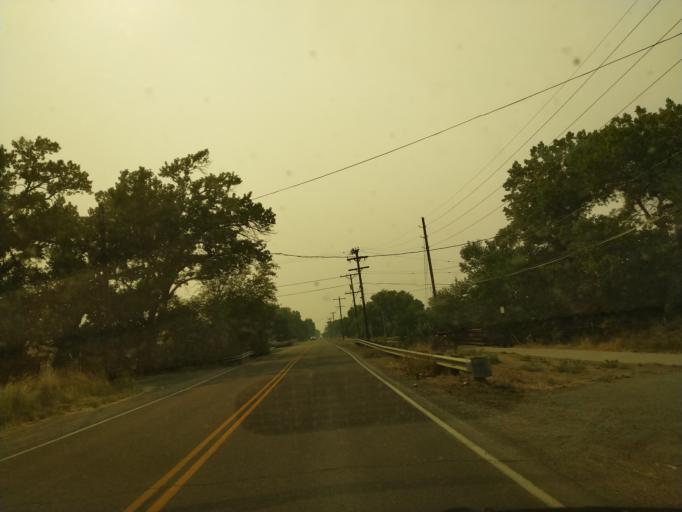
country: US
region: Colorado
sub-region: Mesa County
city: Fruitvale
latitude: 39.0846
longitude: -108.4772
